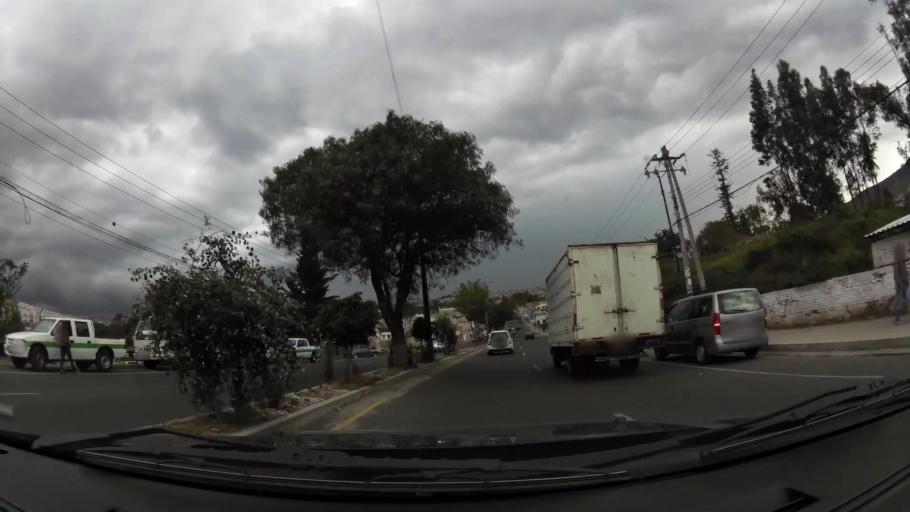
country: EC
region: Pichincha
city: Quito
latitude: -0.0569
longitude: -78.4550
